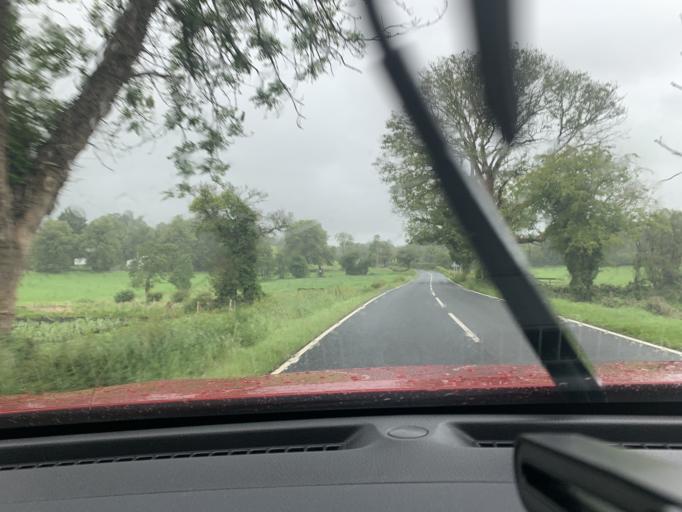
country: GB
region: Northern Ireland
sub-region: Fermanagh District
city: Enniskillen
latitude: 54.3030
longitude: -7.6902
